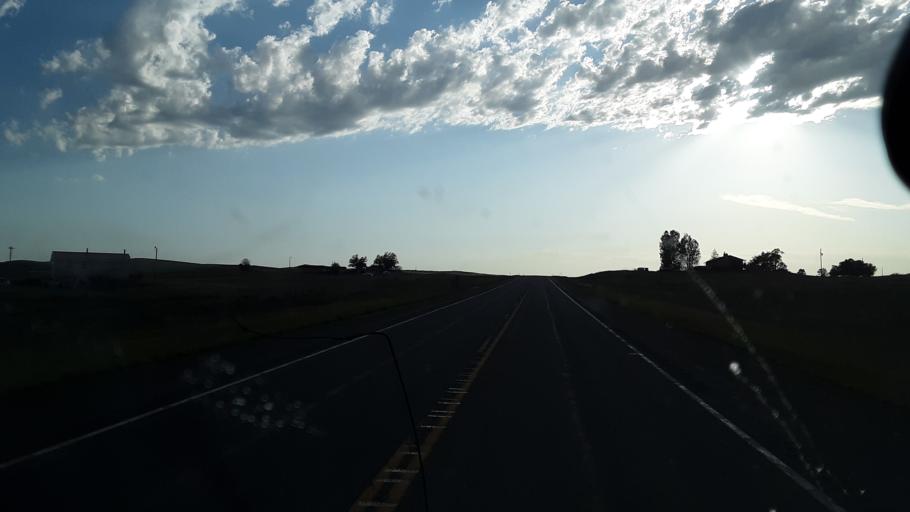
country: US
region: Montana
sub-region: Rosebud County
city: Lame Deer
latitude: 45.5282
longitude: -106.9776
